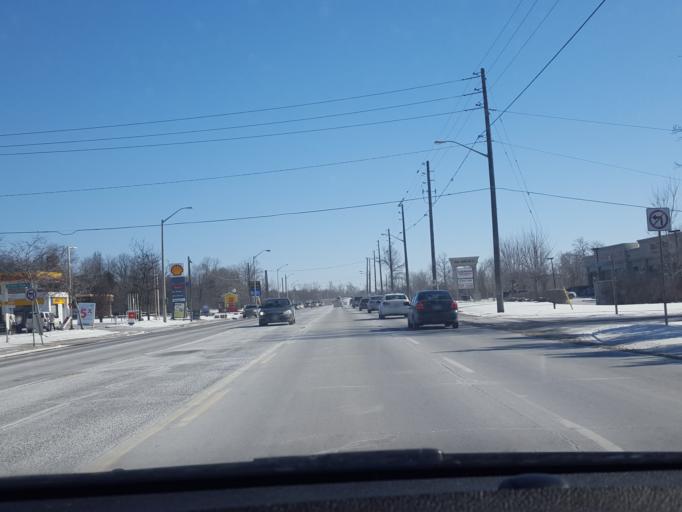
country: CA
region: Ontario
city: Cambridge
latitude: 43.4045
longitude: -80.3865
